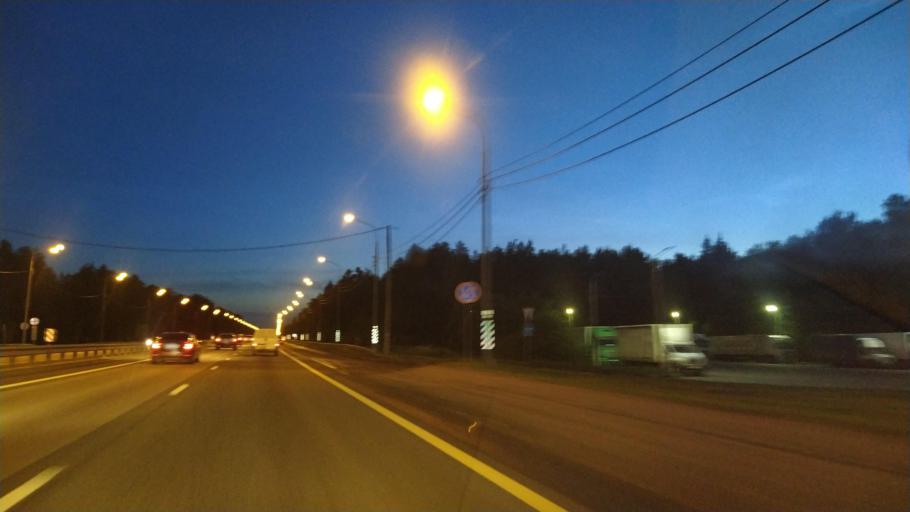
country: RU
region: Leningrad
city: Yanino Vtoroye
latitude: 59.8887
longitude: 30.5890
